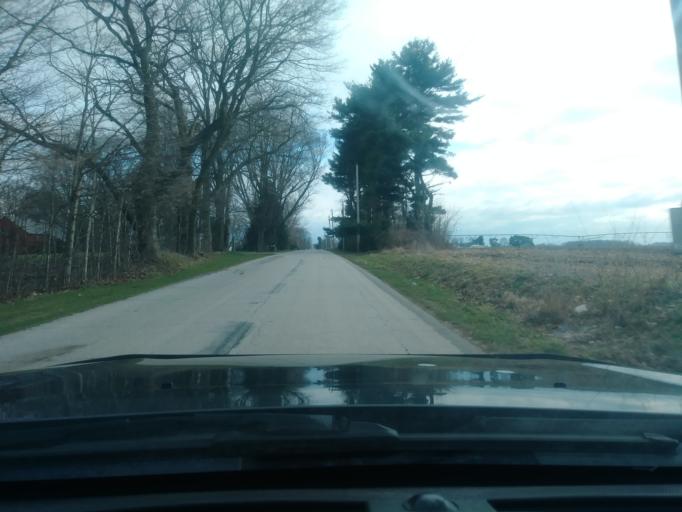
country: US
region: Indiana
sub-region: LaPorte County
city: LaPorte
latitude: 41.5743
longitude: -86.7982
